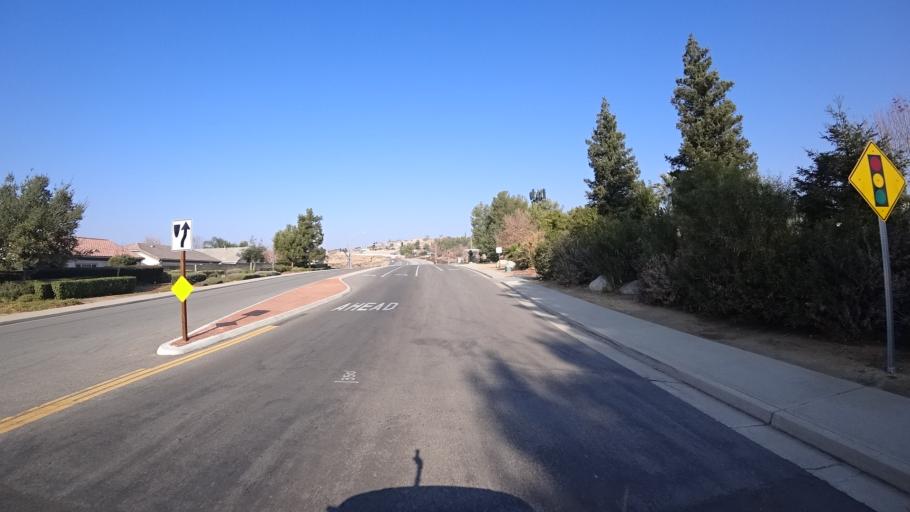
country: US
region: California
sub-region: Kern County
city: Lamont
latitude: 35.4114
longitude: -118.8436
